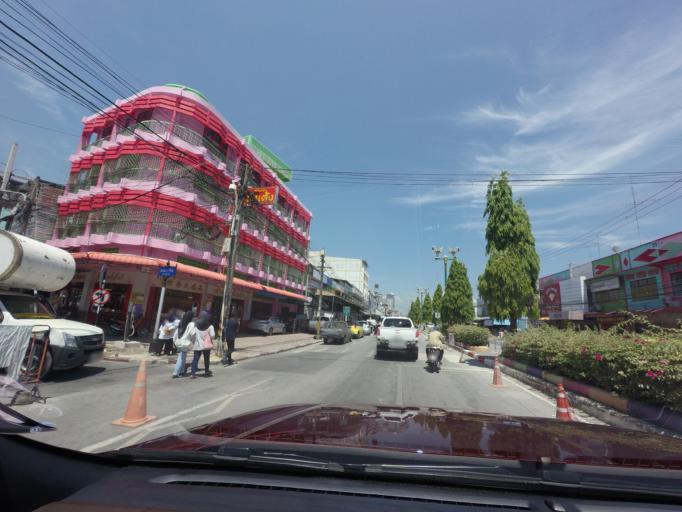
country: TH
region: Yala
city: Yala
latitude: 6.5613
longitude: 101.2911
